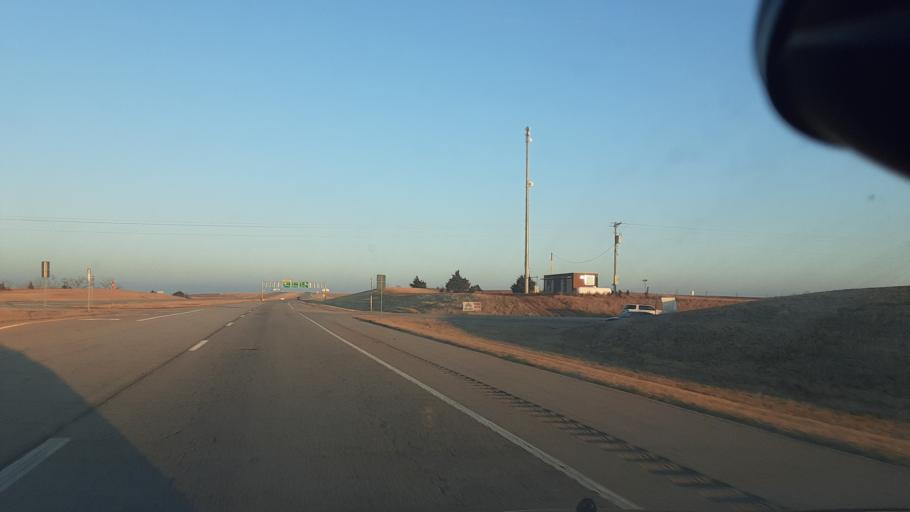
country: US
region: Oklahoma
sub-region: Noble County
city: Perry
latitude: 36.3998
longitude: -97.3375
